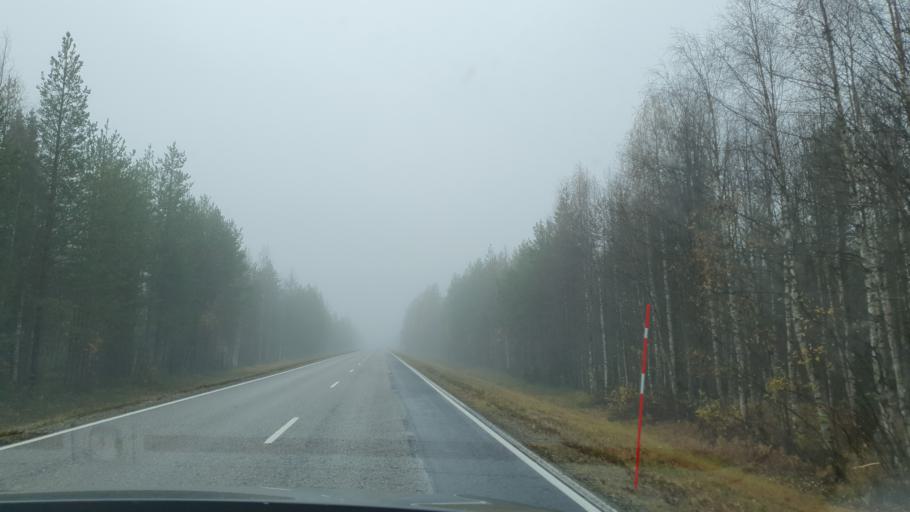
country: FI
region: Lapland
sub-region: Tunturi-Lappi
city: Kittilae
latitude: 67.2251
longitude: 24.9232
